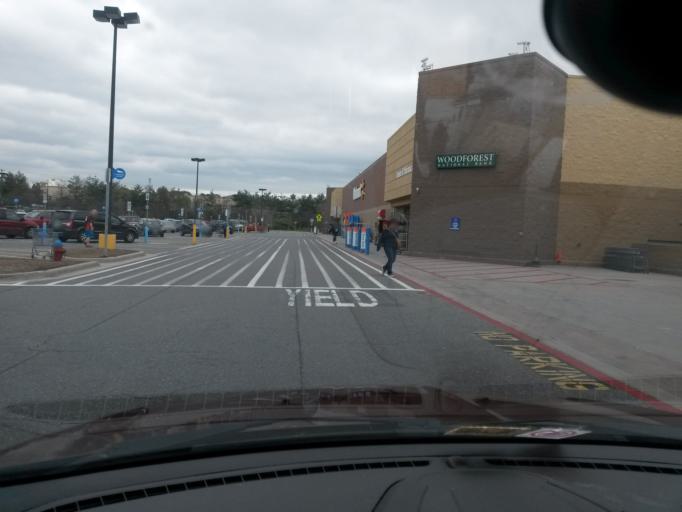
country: US
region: Virginia
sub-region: Montgomery County
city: Merrimac
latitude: 37.1614
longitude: -80.4255
